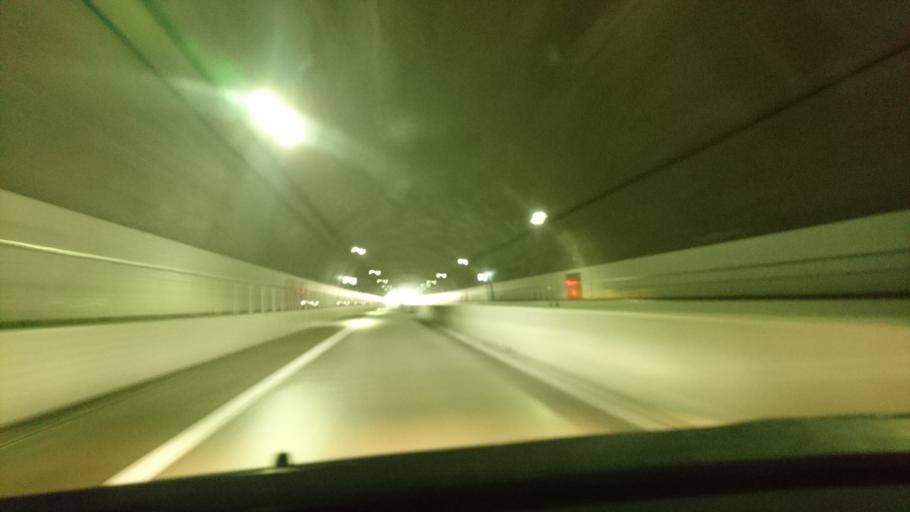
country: JP
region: Iwate
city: Miyako
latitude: 39.8154
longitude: 141.9594
